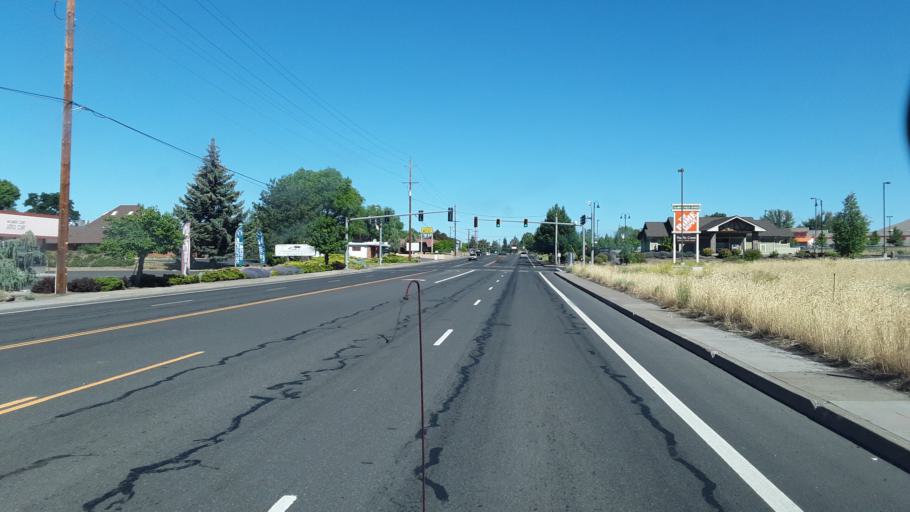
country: US
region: Oregon
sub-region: Klamath County
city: Altamont
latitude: 42.2029
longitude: -121.7078
